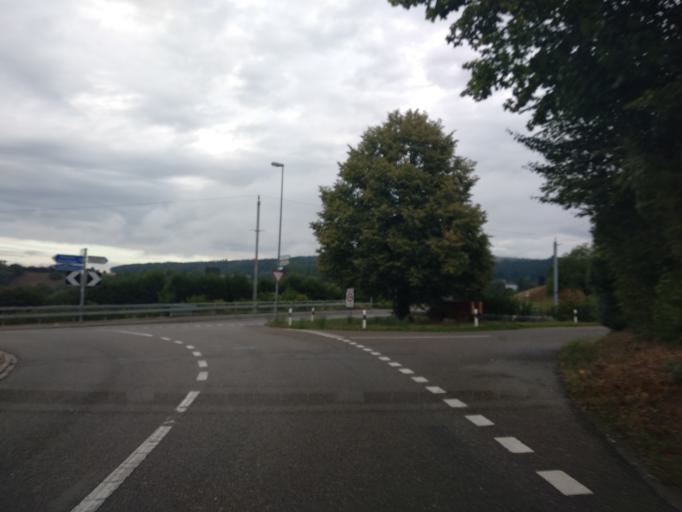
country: CH
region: Thurgau
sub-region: Frauenfeld District
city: Diessenhofen
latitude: 47.6876
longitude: 8.7342
